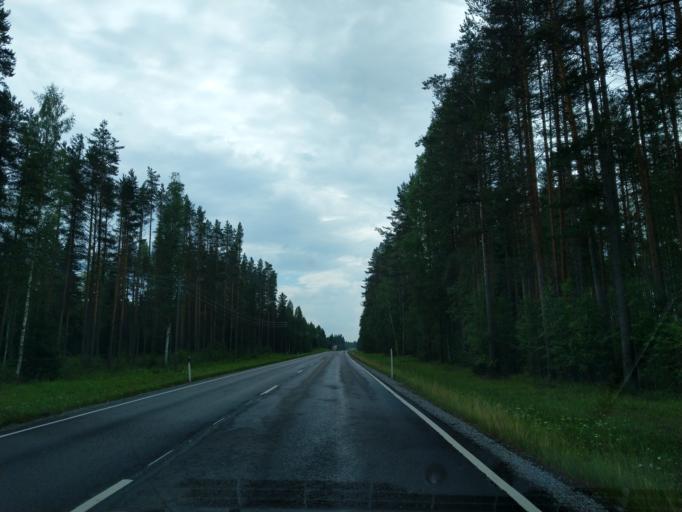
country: FI
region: Southern Savonia
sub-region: Savonlinna
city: Punkaharju
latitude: 61.6515
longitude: 29.4216
